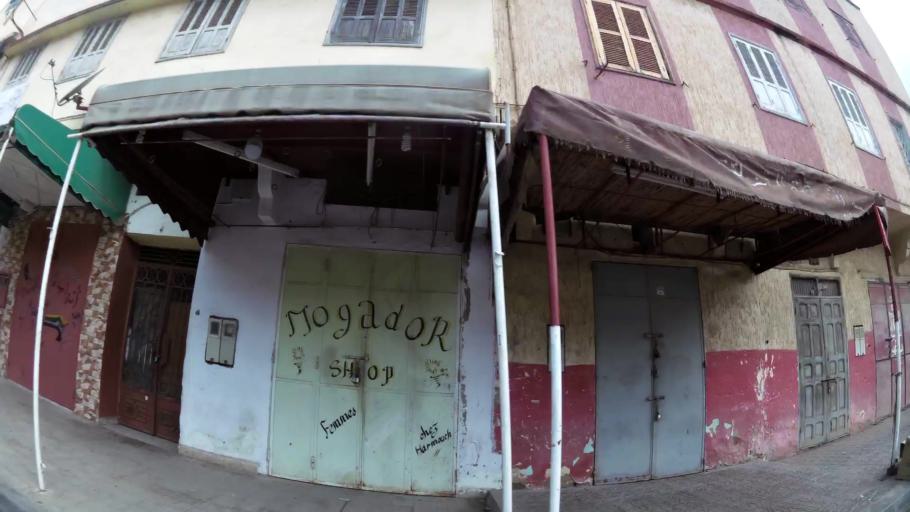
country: MA
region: Rabat-Sale-Zemmour-Zaer
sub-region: Khemisset
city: Tiflet
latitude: 33.8943
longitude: -6.3105
